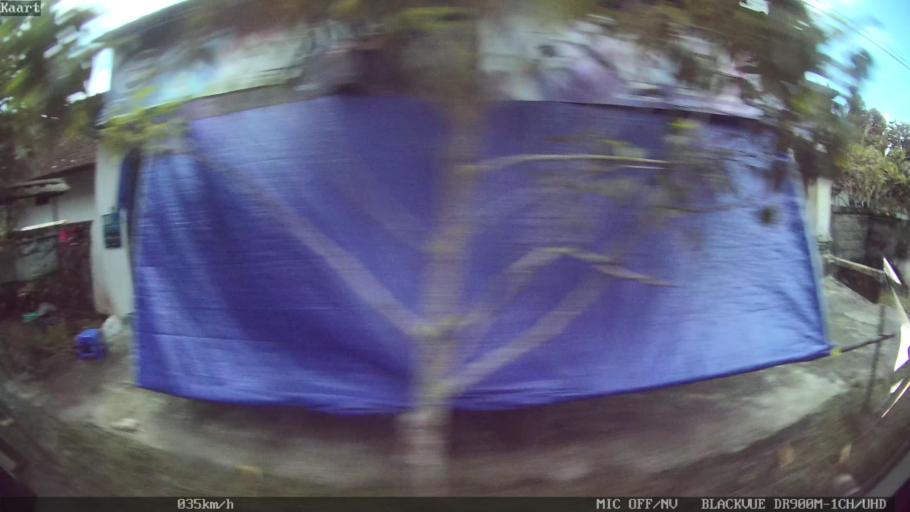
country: ID
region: Bali
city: Banjar Petak
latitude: -8.4495
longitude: 115.3186
